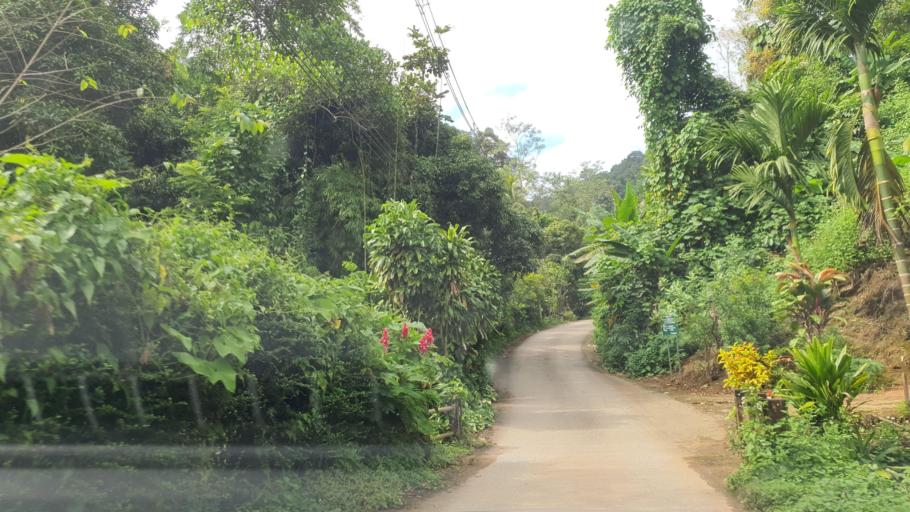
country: TH
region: Chiang Mai
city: Mae On
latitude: 18.9381
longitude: 99.3097
